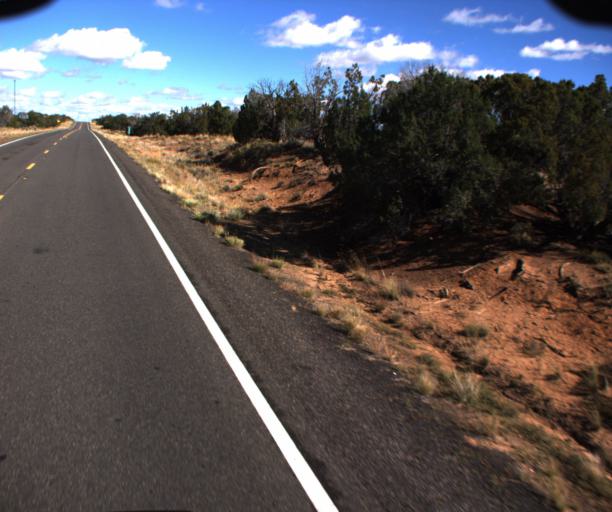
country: US
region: Arizona
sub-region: Apache County
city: Saint Johns
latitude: 34.8352
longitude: -109.2375
